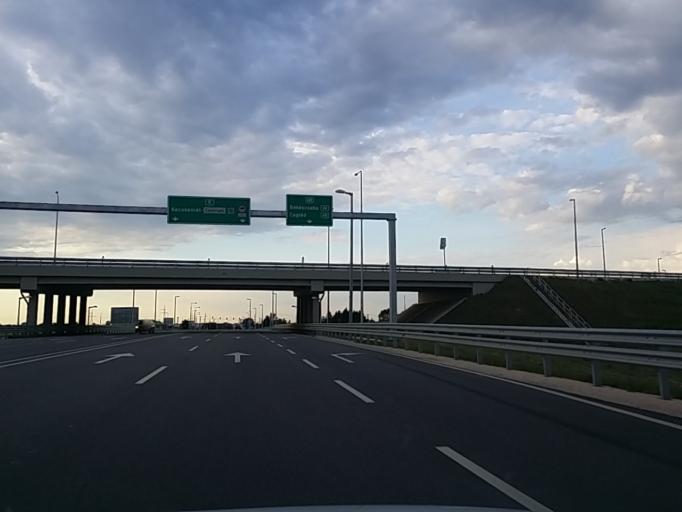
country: HU
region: Bacs-Kiskun
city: Kecskemet
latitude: 46.9413
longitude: 19.6581
